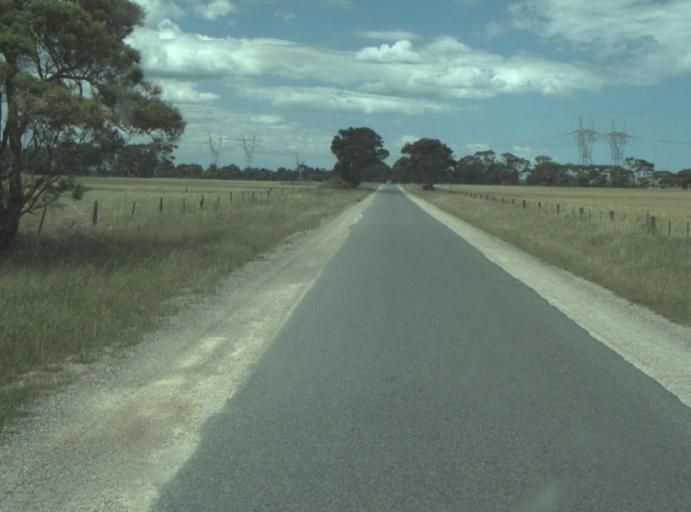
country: AU
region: Victoria
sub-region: Wyndham
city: Little River
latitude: -37.8757
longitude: 144.3989
